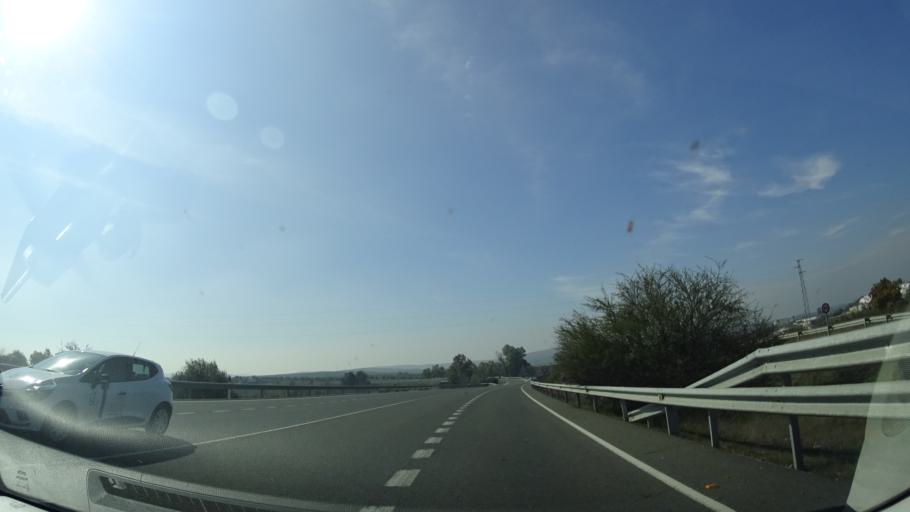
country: ES
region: Andalusia
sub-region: Province of Cordoba
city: Montoro
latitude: 38.0135
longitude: -4.3702
